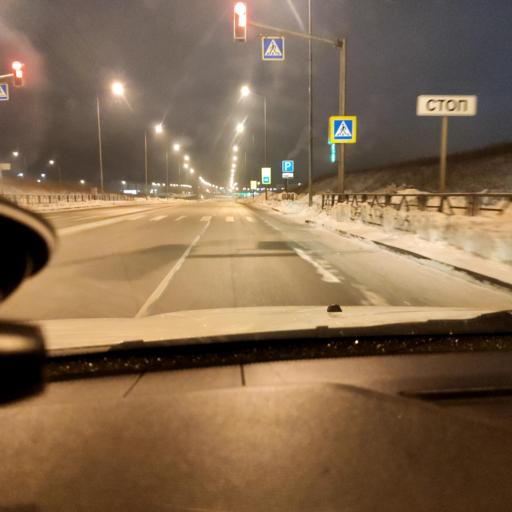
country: RU
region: Samara
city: Petra-Dubrava
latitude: 53.3069
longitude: 50.3376
